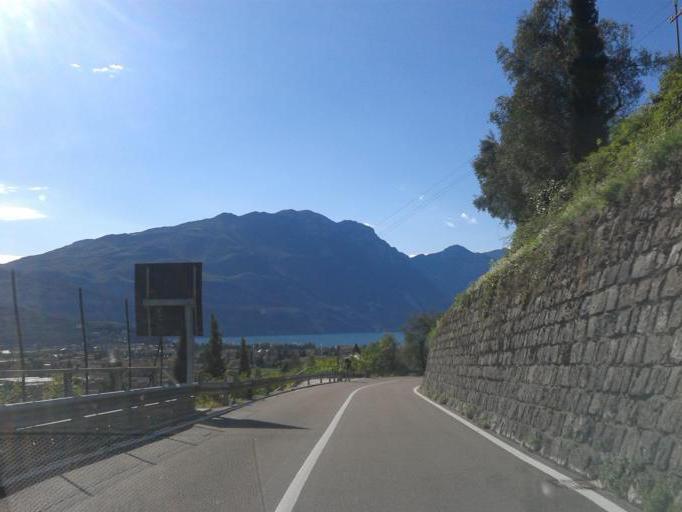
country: IT
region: Trentino-Alto Adige
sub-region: Provincia di Trento
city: Riva del Garda
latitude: 45.9011
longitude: 10.8343
